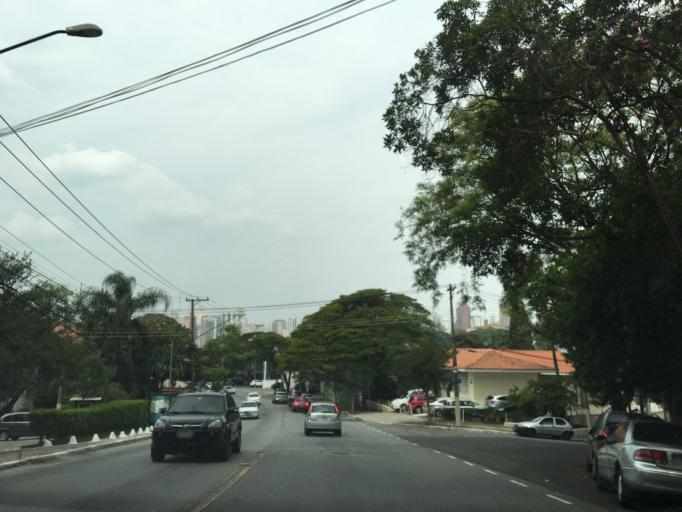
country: BR
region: Sao Paulo
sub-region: Sao Paulo
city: Sao Paulo
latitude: -23.5483
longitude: -46.6733
